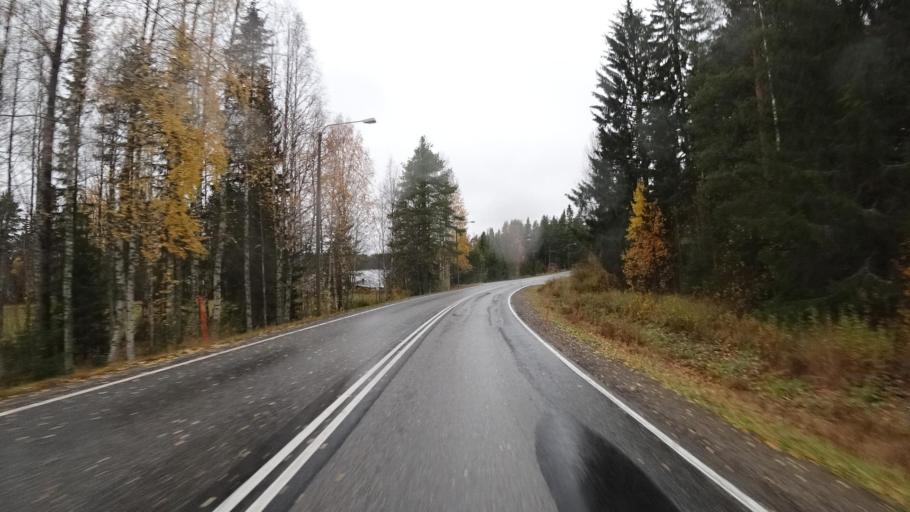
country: FI
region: Northern Savo
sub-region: Koillis-Savo
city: Tuusniemi
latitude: 62.7932
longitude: 28.5499
